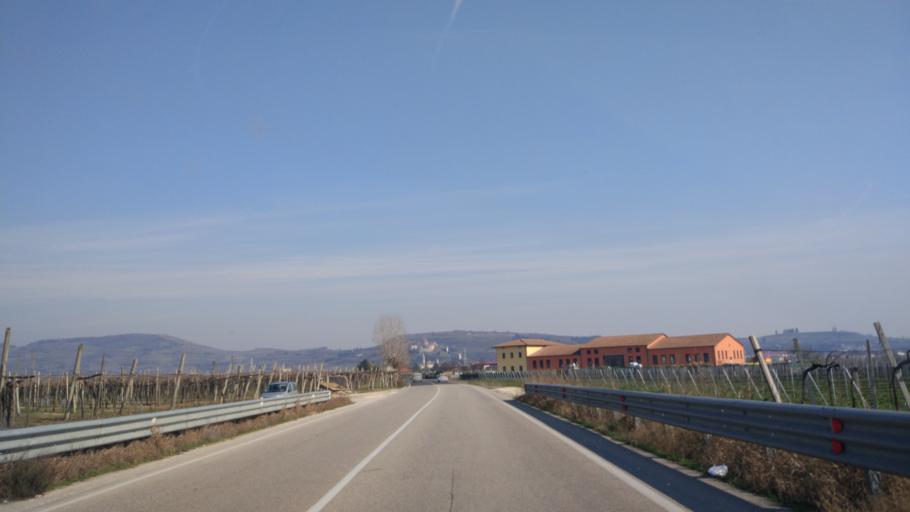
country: IT
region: Veneto
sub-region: Provincia di Verona
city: Soave
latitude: 45.4128
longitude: 11.2262
